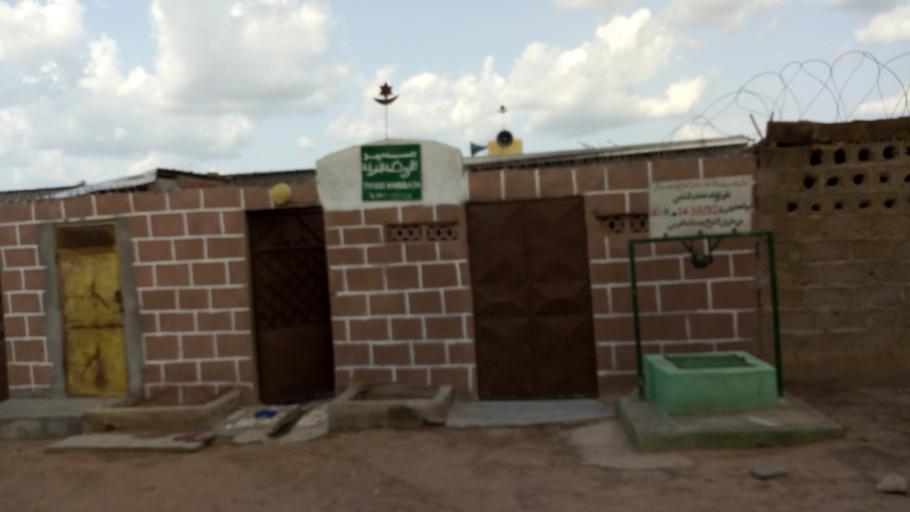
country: CI
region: Vallee du Bandama
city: Bouake
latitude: 7.7170
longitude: -5.0181
